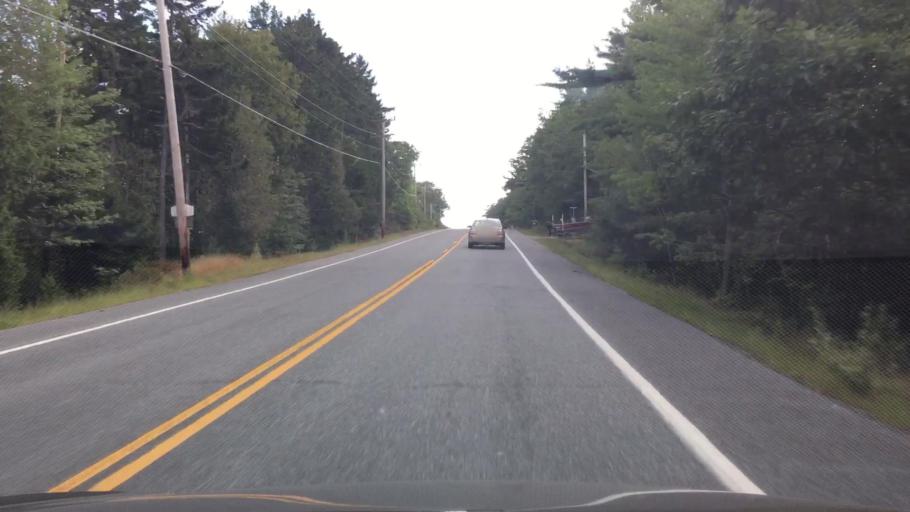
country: US
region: Maine
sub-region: Hancock County
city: Surry
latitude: 44.4528
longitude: -68.5548
